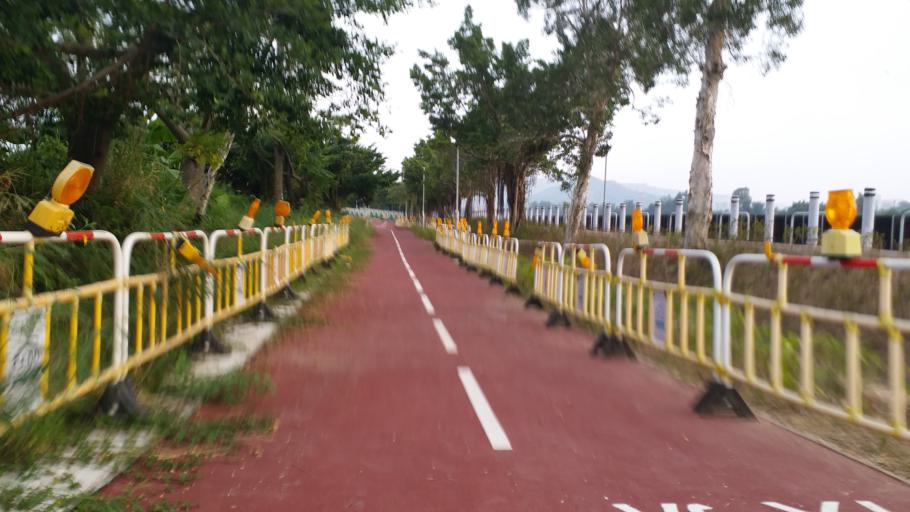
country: HK
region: Yuen Long
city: Yuen Long Kau Hui
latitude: 22.4613
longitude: 114.0464
